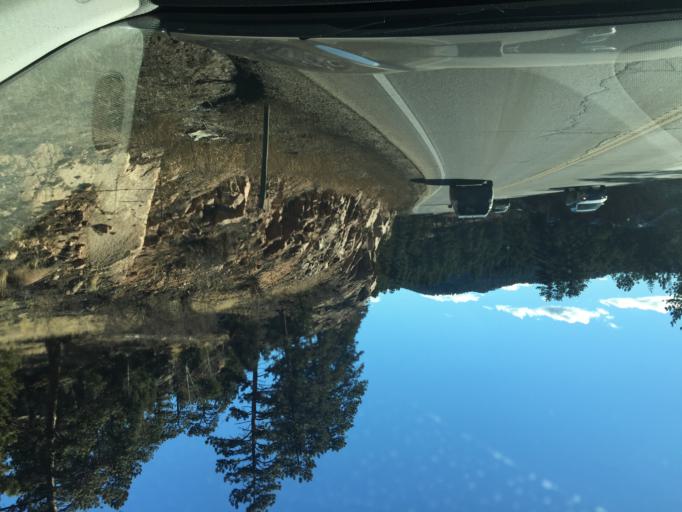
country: US
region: Colorado
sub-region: Jefferson County
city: Evergreen
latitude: 39.4848
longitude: -105.3621
